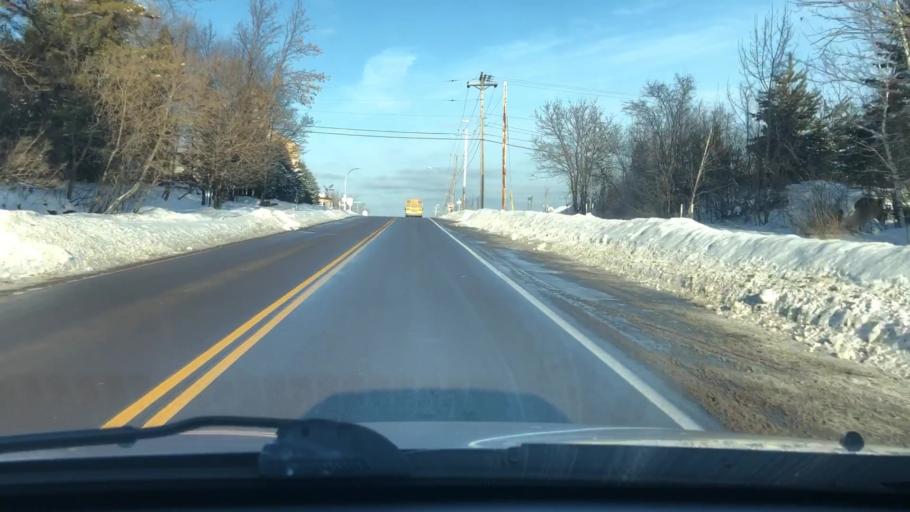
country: US
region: Minnesota
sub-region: Saint Louis County
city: Duluth
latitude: 46.8149
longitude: -92.0697
